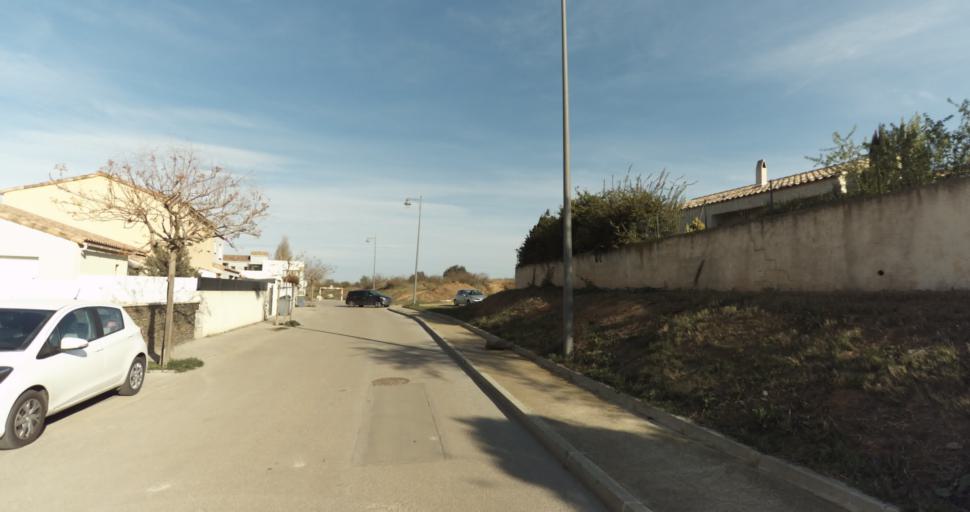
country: FR
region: Languedoc-Roussillon
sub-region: Departement de l'Herault
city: Marseillan
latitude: 43.3627
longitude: 3.5240
